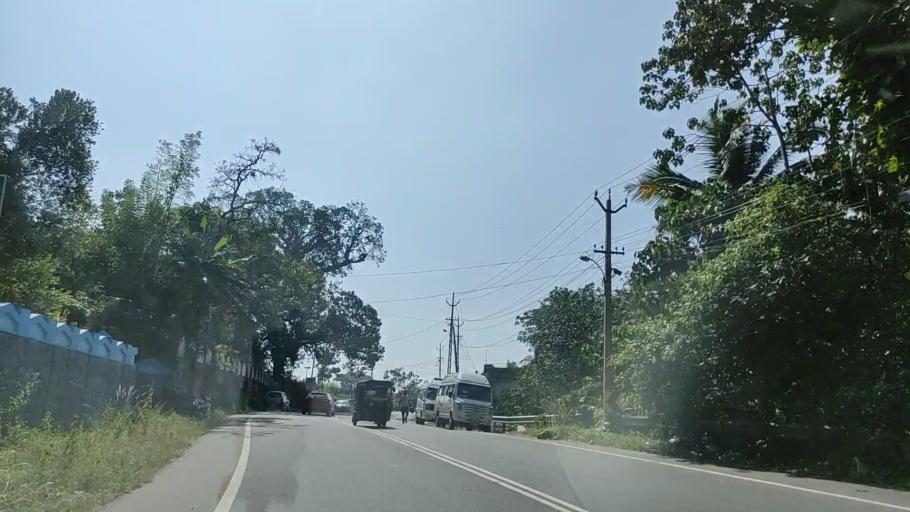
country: IN
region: Kerala
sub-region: Kollam
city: Punalur
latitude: 8.9083
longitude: 77.0532
